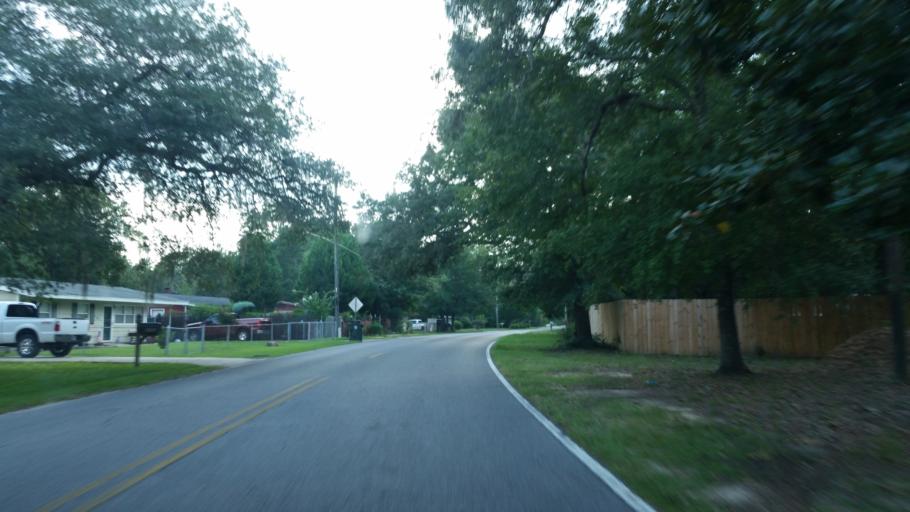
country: US
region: Florida
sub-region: Santa Rosa County
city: Milton
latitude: 30.6253
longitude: -87.0493
